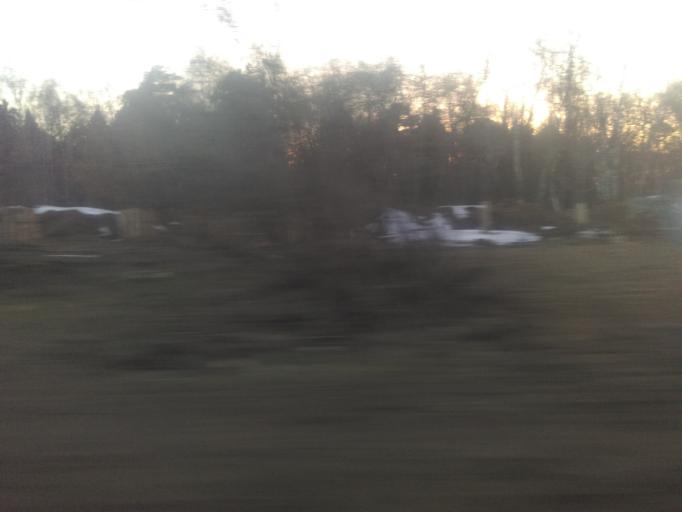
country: RU
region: Moscow
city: Mikhalkovo
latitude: 55.6924
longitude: 37.4256
